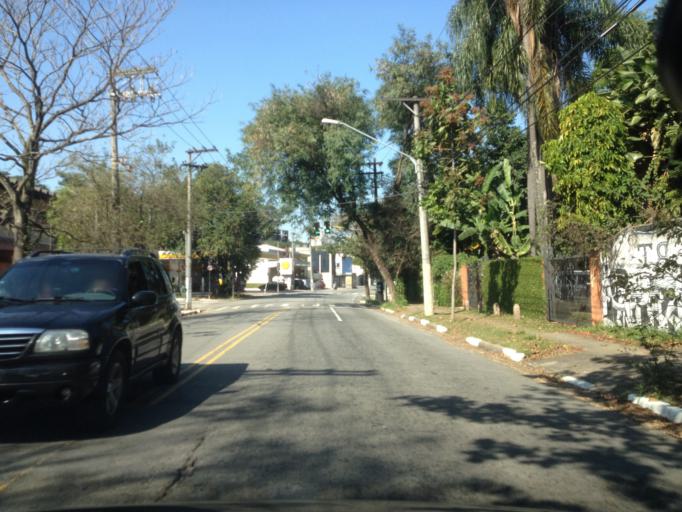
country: BR
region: Sao Paulo
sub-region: Sao Paulo
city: Sao Paulo
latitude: -23.5550
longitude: -46.7012
